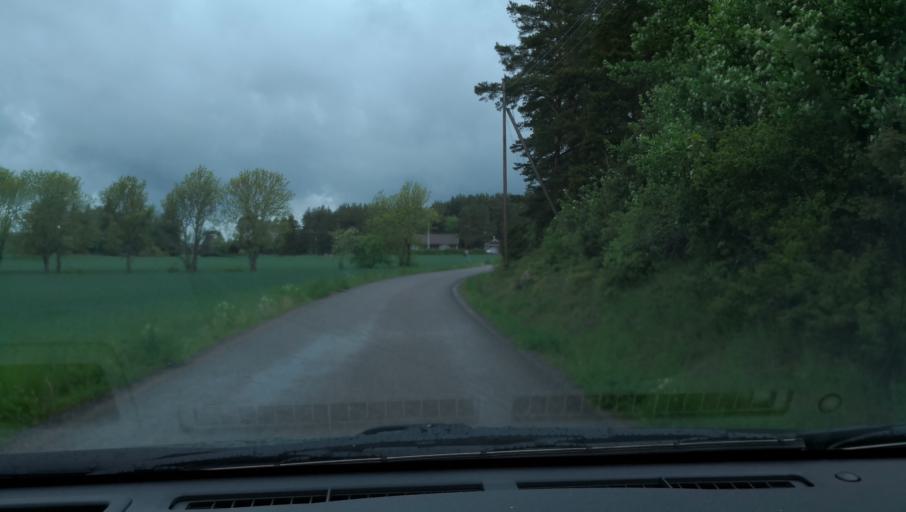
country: SE
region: Uppsala
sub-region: Enkopings Kommun
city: Orsundsbro
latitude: 59.8082
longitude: 17.3806
